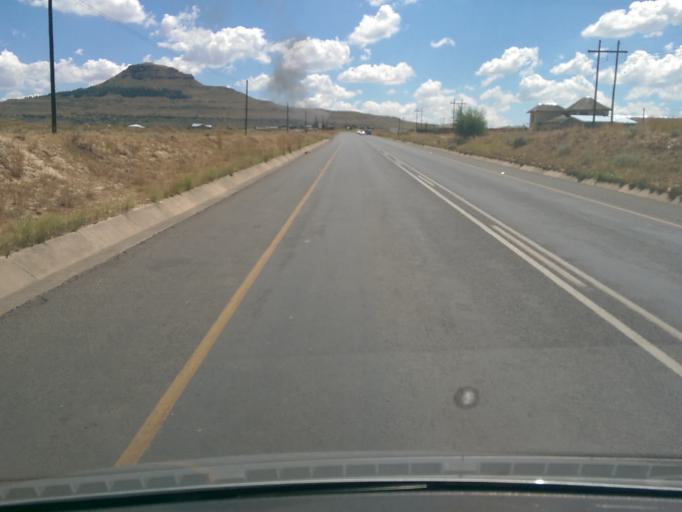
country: LS
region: Maseru
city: Maseru
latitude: -29.3761
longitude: 27.4817
